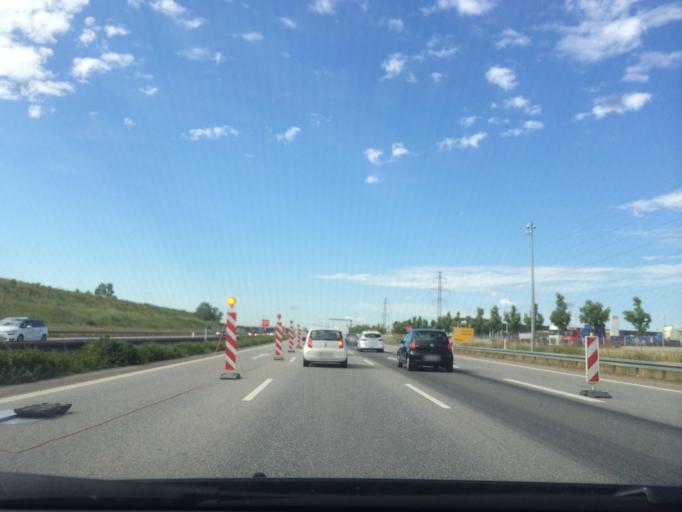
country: DK
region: Zealand
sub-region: Greve Kommune
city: Greve
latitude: 55.5882
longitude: 12.2673
